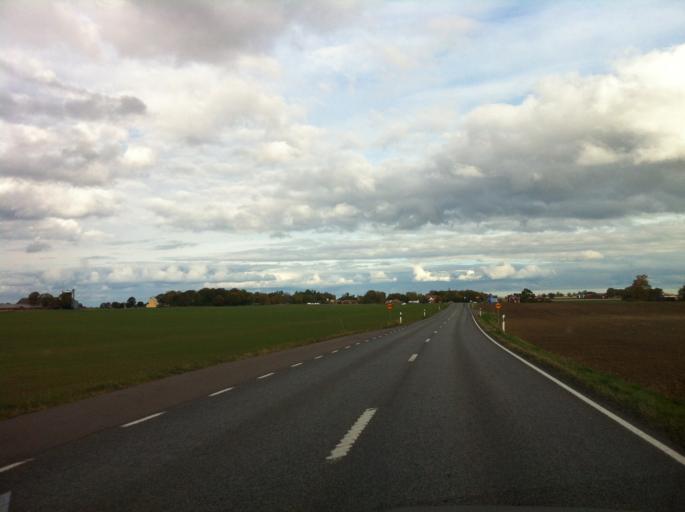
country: SE
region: OEstergoetland
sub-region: Vadstena Kommun
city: Herrestad
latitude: 58.3738
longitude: 14.7360
